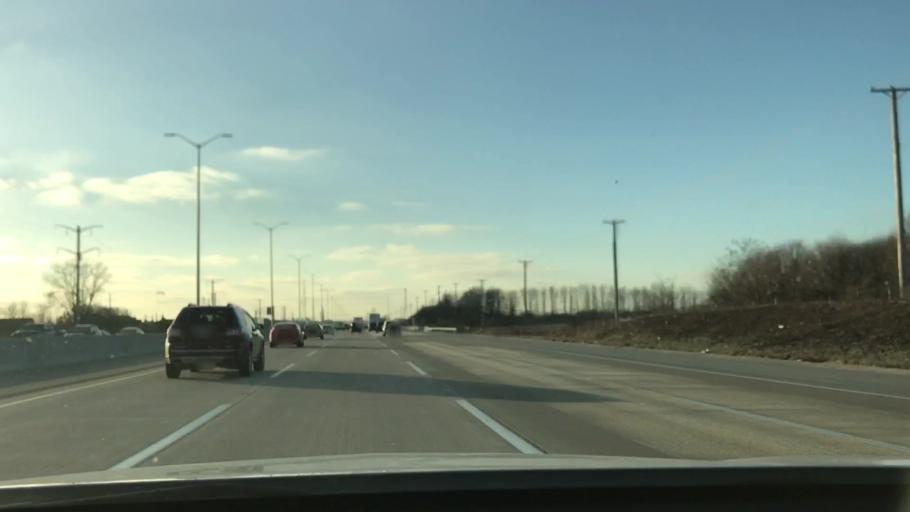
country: US
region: Illinois
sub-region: Kane County
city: East Dundee
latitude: 42.0669
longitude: -88.2270
